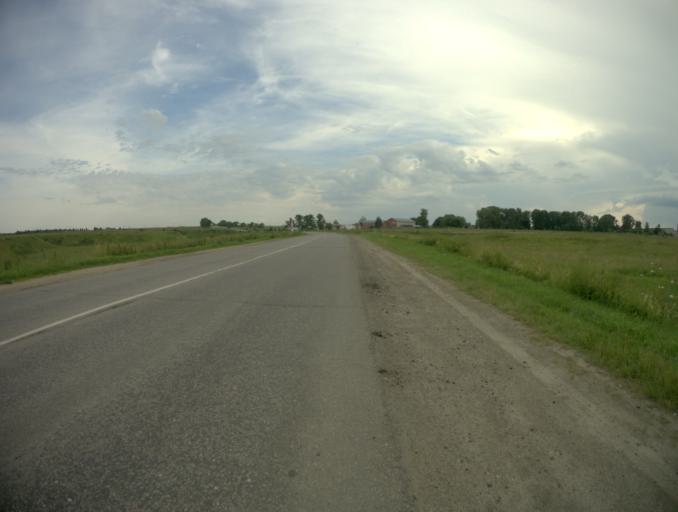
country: RU
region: Vladimir
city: Suzdal'
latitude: 56.4055
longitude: 40.4456
